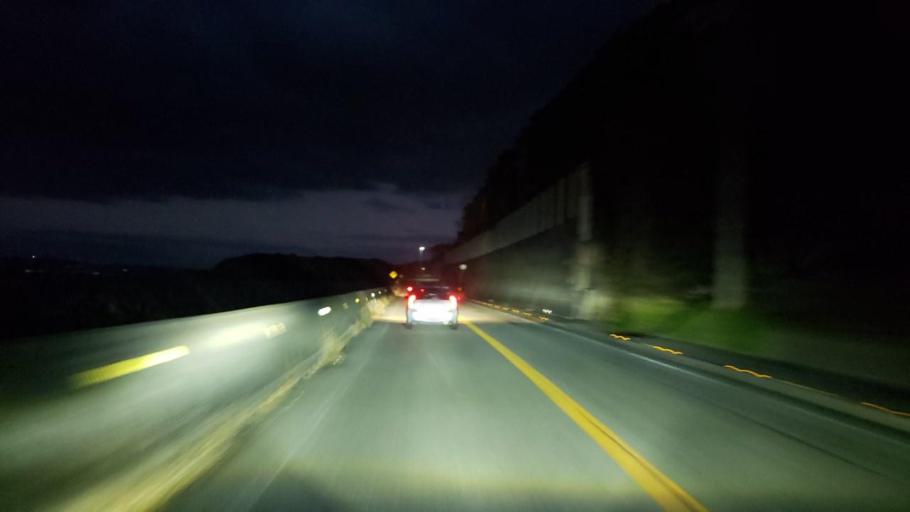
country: JP
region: Tokushima
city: Narutocho-mitsuishi
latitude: 34.2261
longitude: 134.5380
